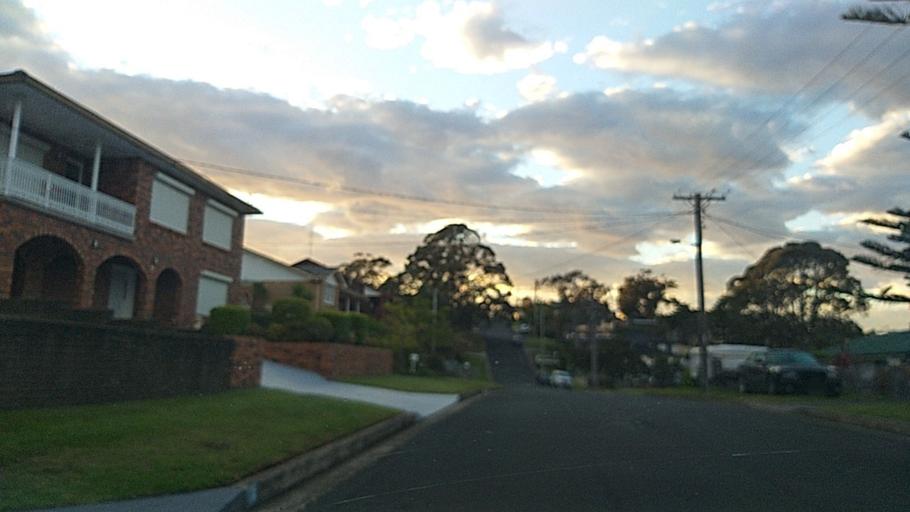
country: AU
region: New South Wales
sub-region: Wollongong
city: Koonawarra
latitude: -34.4925
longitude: 150.8117
